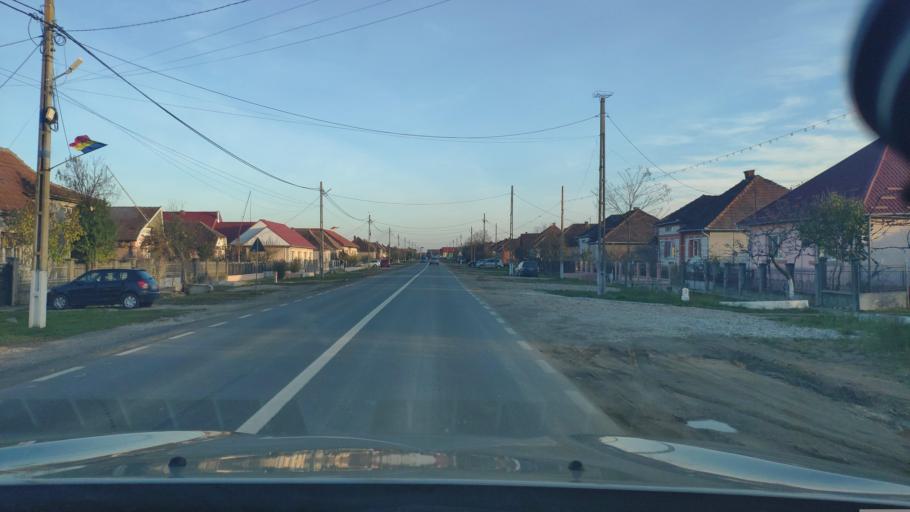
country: RO
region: Satu Mare
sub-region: Comuna Mediesu Aurit
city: Potau
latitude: 47.7764
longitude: 23.0959
